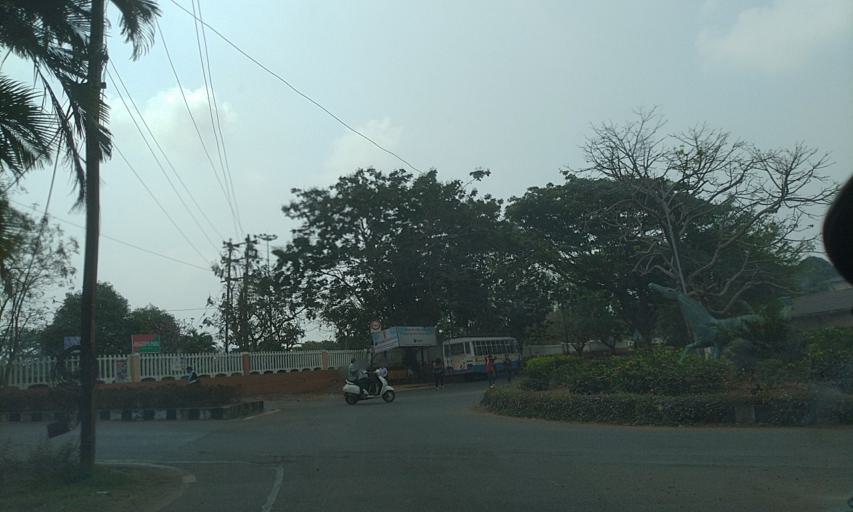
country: IN
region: Goa
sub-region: North Goa
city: Panaji
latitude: 15.4877
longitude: 73.8262
